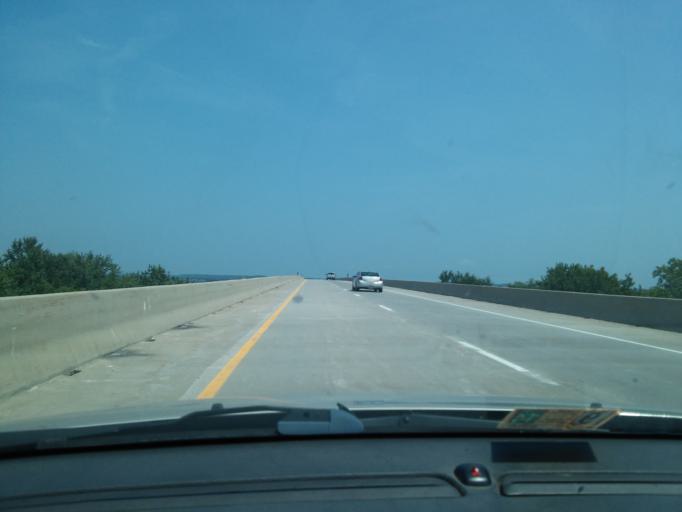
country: US
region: Illinois
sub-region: Pike County
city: Griggsville
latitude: 39.6858
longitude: -90.6435
